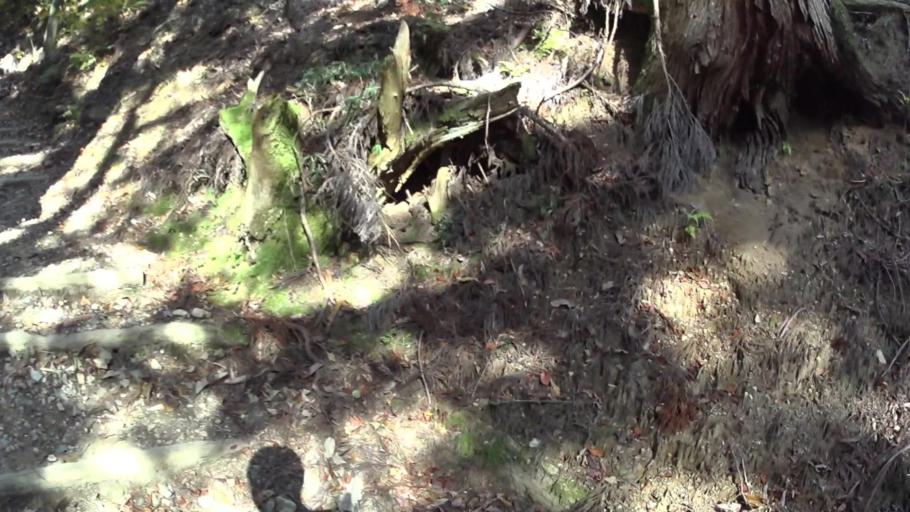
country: JP
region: Kyoto
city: Kameoka
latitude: 35.0477
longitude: 135.6370
